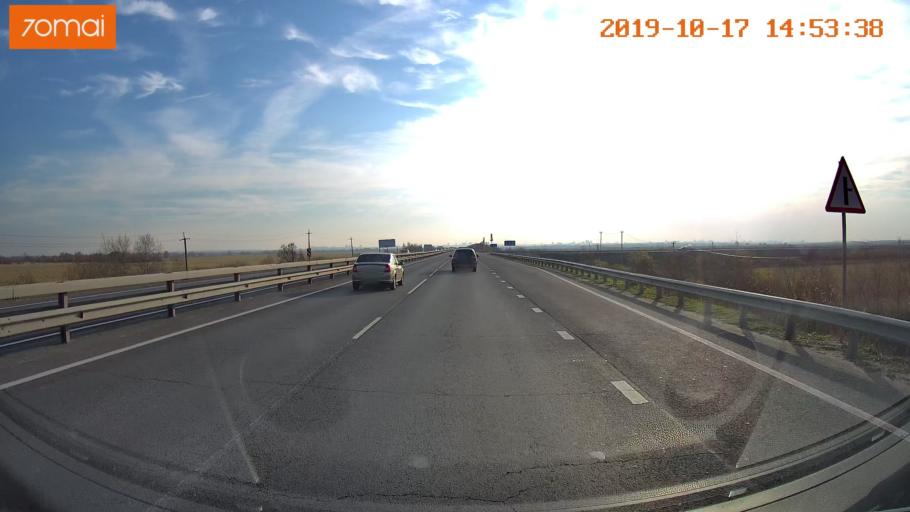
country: RU
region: Rjazan
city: Polyany
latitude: 54.6912
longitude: 39.8370
